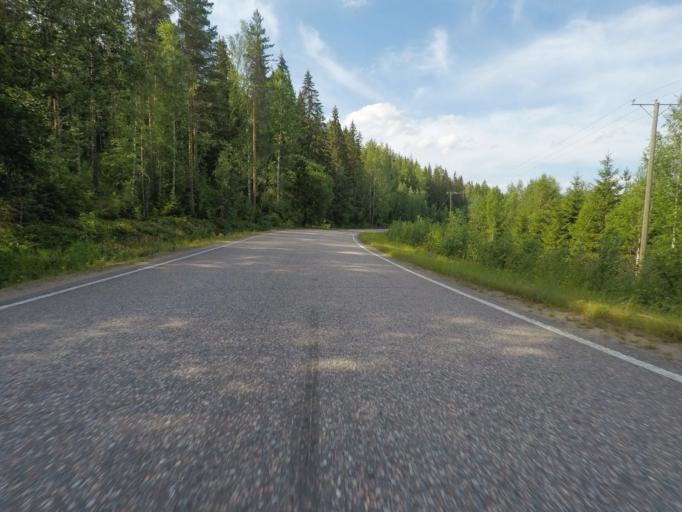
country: FI
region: Southern Savonia
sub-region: Savonlinna
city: Sulkava
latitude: 61.7255
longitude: 28.2051
